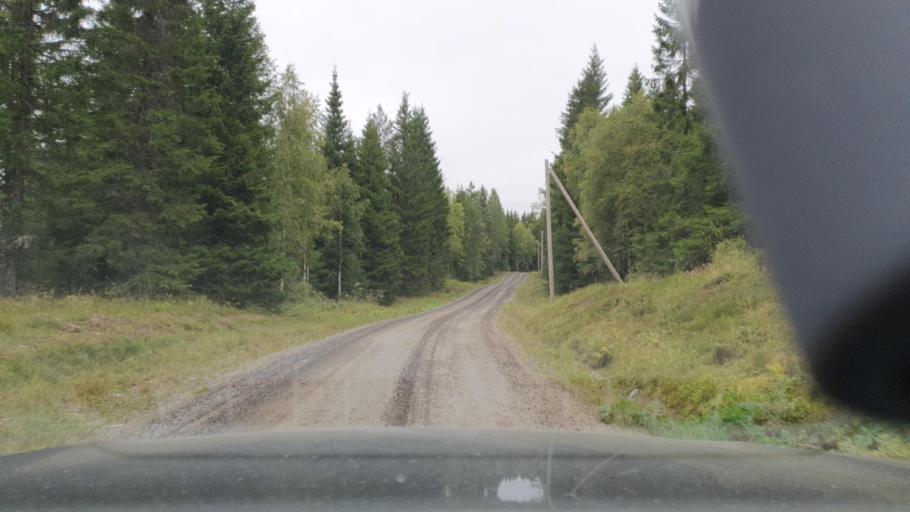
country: SE
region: Vaermland
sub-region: Eda Kommun
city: Charlottenberg
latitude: 60.1588
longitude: 12.6017
